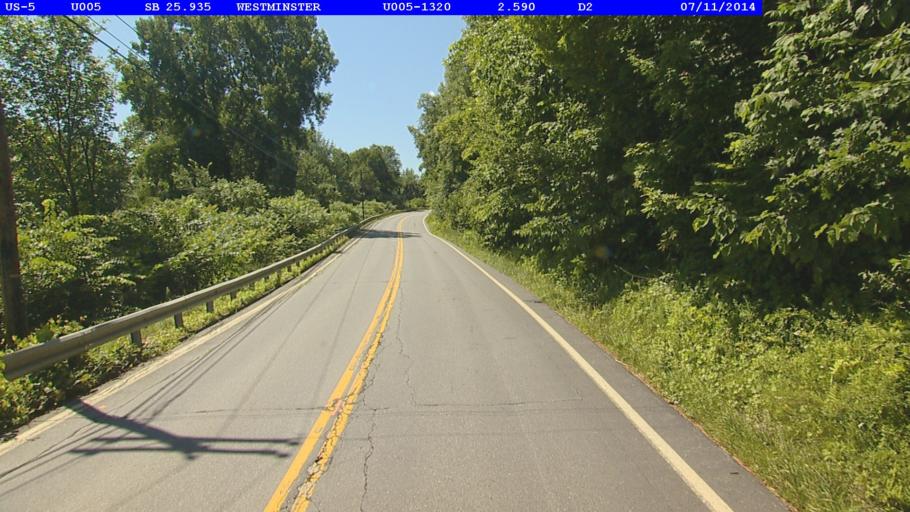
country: US
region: Vermont
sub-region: Windham County
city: Bellows Falls
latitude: 43.0562
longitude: -72.4694
